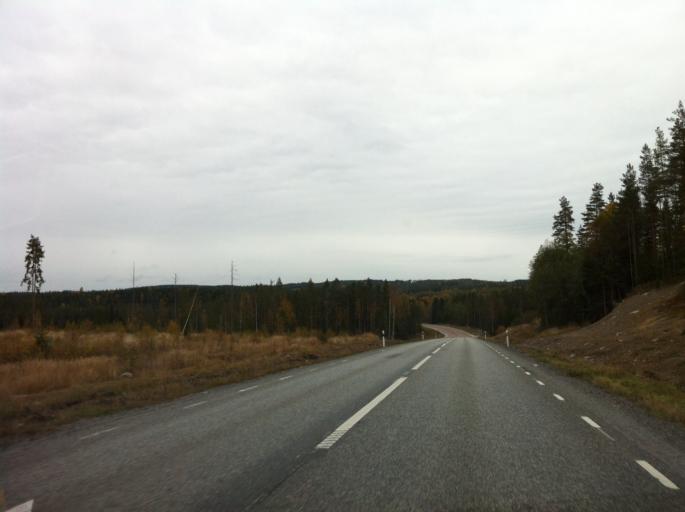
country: SE
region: OErebro
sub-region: Ljusnarsbergs Kommun
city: Kopparberg
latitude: 59.9808
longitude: 15.0207
